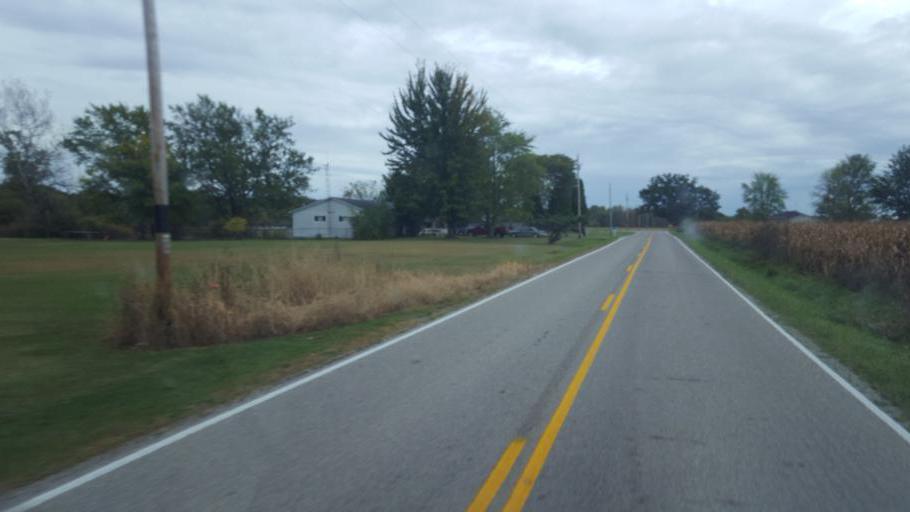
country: US
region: Ohio
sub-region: Huron County
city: Wakeman
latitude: 41.1854
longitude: -82.4302
